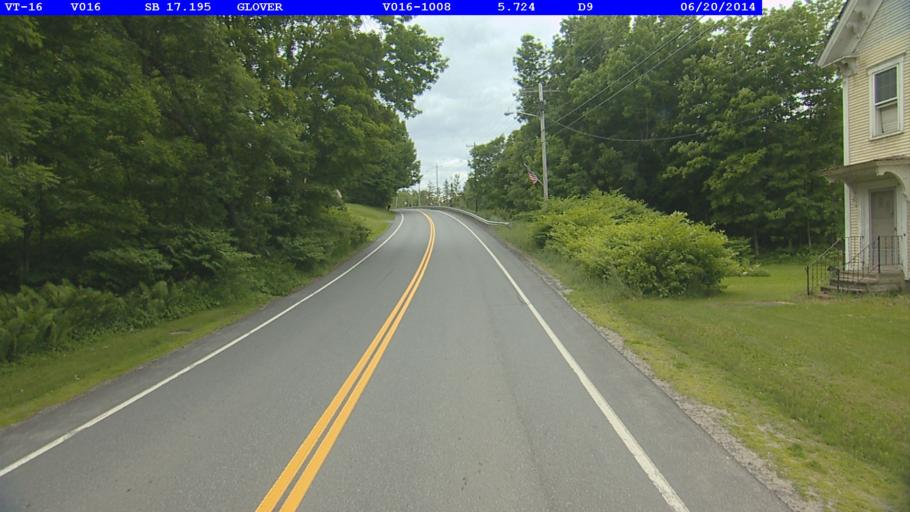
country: US
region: Vermont
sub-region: Orleans County
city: Newport
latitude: 44.7038
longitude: -72.1888
